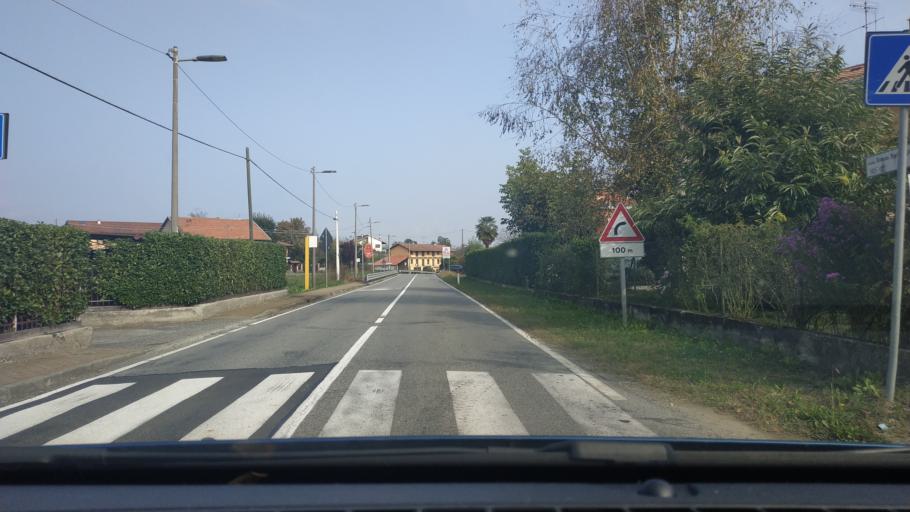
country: IT
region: Piedmont
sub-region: Provincia di Torino
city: Scarmagno
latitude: 45.3629
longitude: 7.8423
